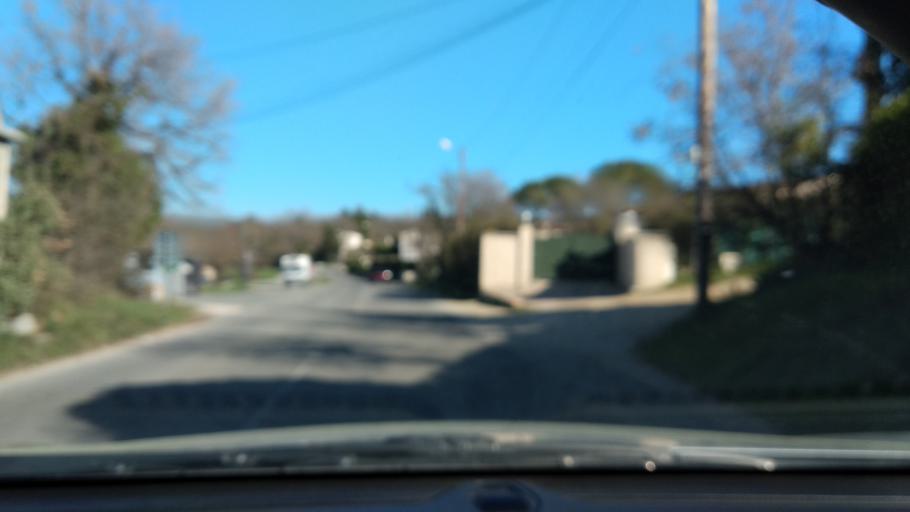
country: FR
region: Provence-Alpes-Cote d'Azur
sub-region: Departement des Alpes-Maritimes
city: Saint-Cezaire-sur-Siagne
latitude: 43.6499
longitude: 6.8033
